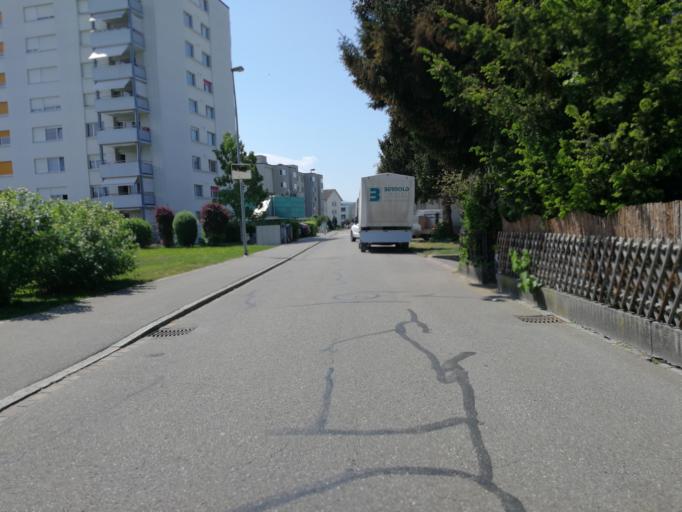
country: CH
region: Saint Gallen
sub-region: Wahlkreis See-Gaster
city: Jona
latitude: 47.2285
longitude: 8.8326
